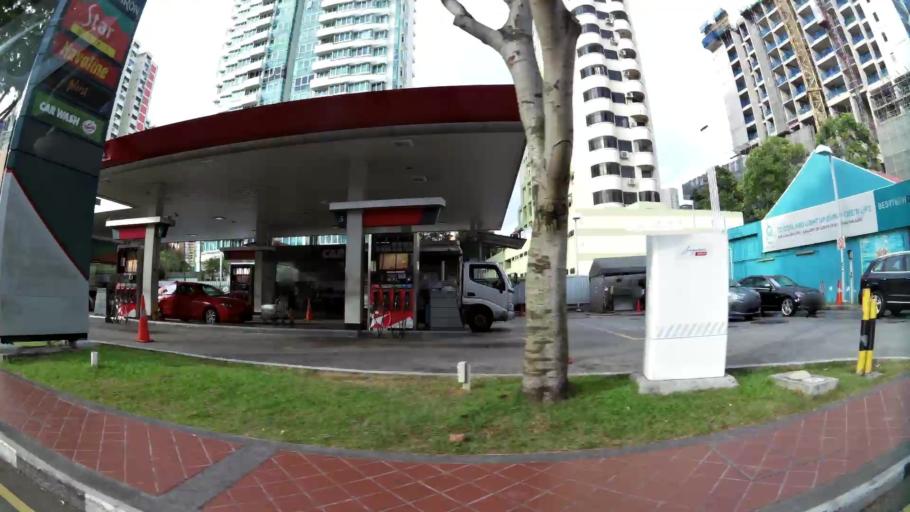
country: SG
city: Singapore
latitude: 1.3266
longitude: 103.8454
